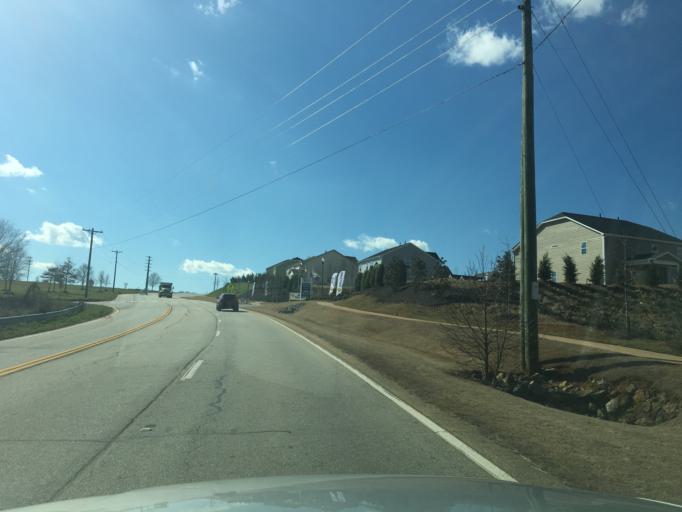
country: US
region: South Carolina
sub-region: Spartanburg County
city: Duncan
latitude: 34.8715
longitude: -82.1620
